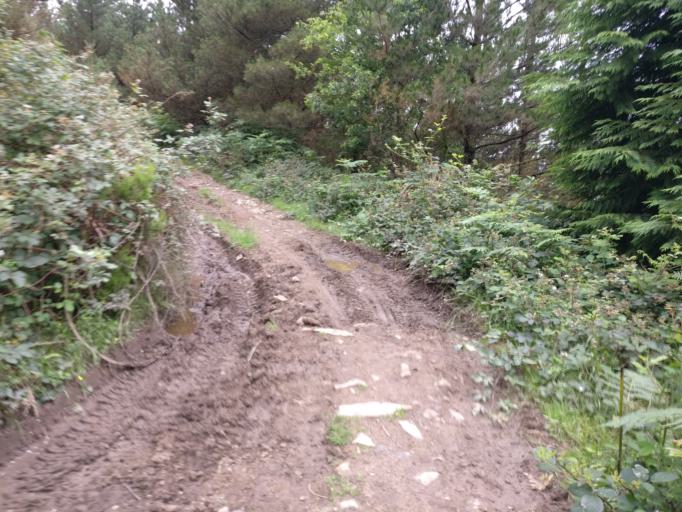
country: ES
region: Basque Country
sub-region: Bizkaia
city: Alonsotegi
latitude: 43.2220
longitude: -2.9492
